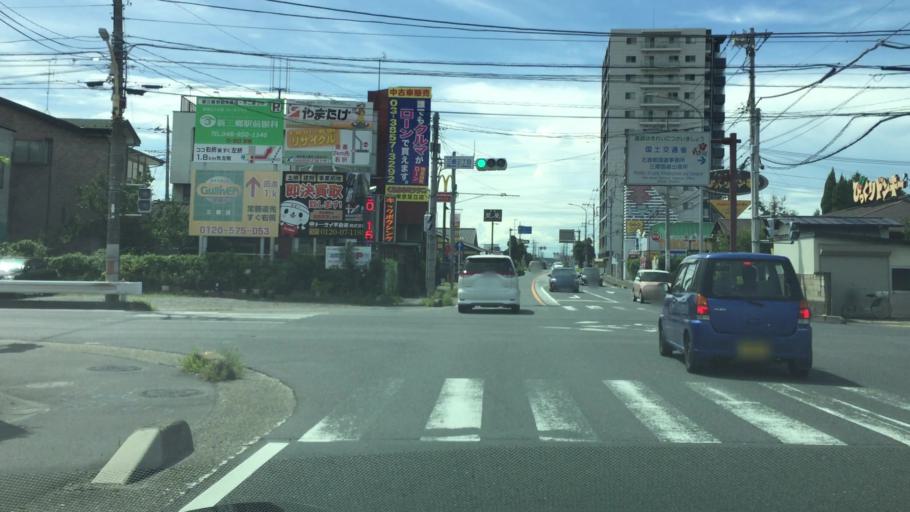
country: JP
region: Chiba
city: Nagareyama
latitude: 35.8461
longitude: 139.8812
